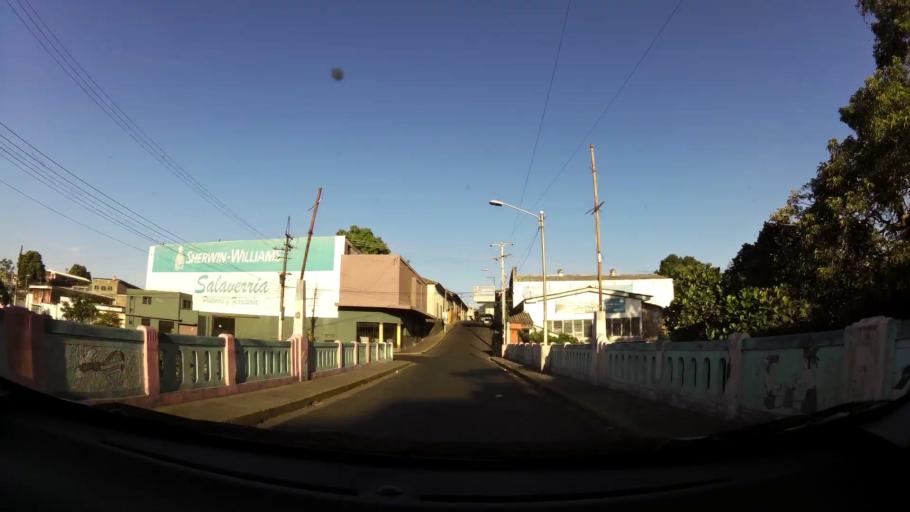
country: SV
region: Sonsonate
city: Sonsonate
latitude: 13.7205
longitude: -89.7251
